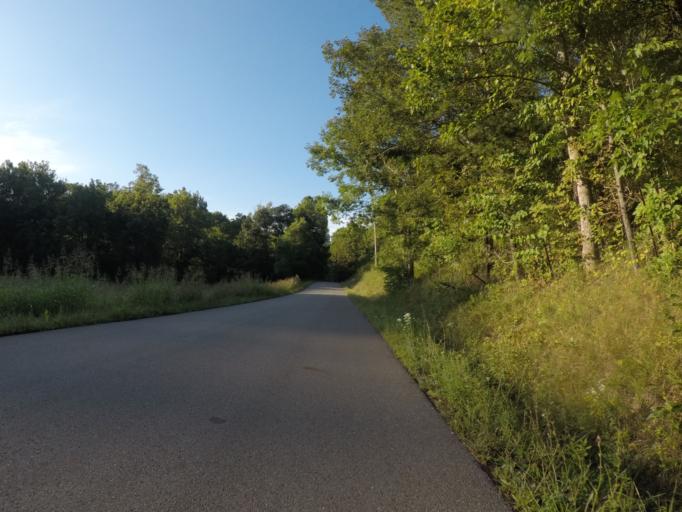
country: US
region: Ohio
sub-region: Lawrence County
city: Coal Grove
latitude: 38.5543
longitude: -82.5536
